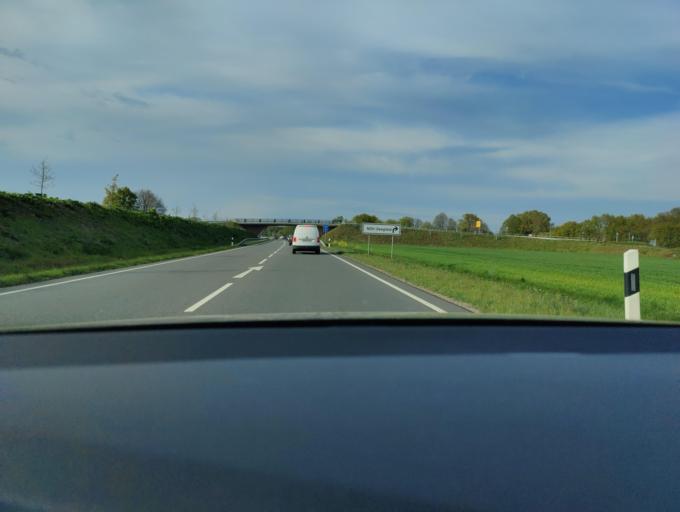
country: DE
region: Lower Saxony
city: Nordhorn
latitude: 52.4481
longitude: 7.0880
